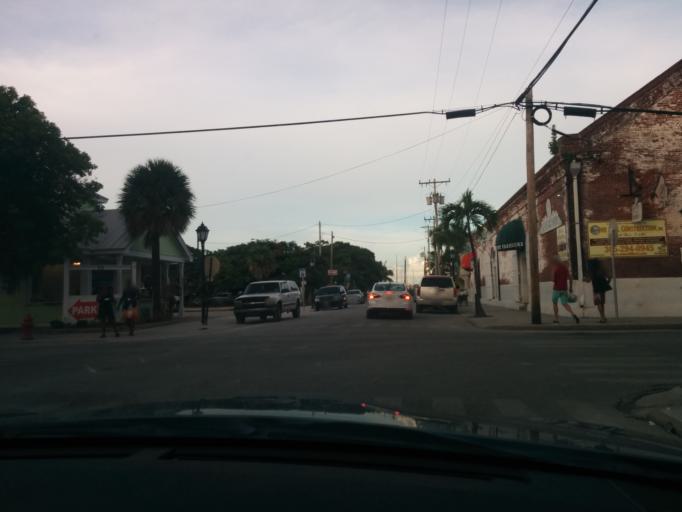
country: US
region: Florida
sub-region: Monroe County
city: Key West
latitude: 24.5598
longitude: -81.8041
